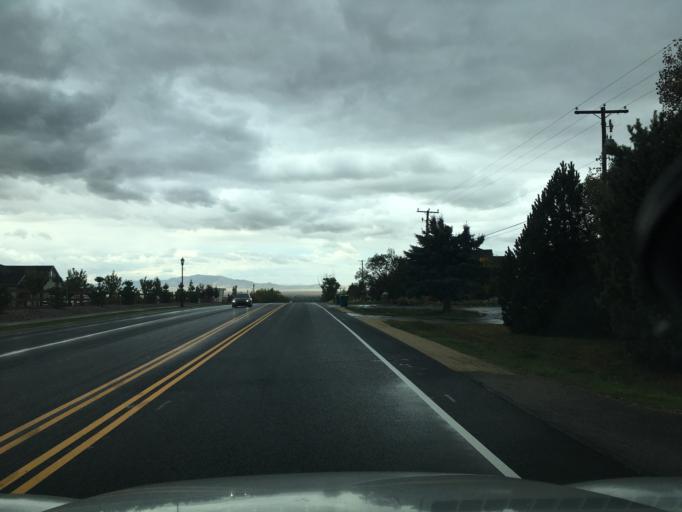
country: US
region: Utah
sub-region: Davis County
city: Fruit Heights
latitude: 41.0659
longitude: -111.9168
